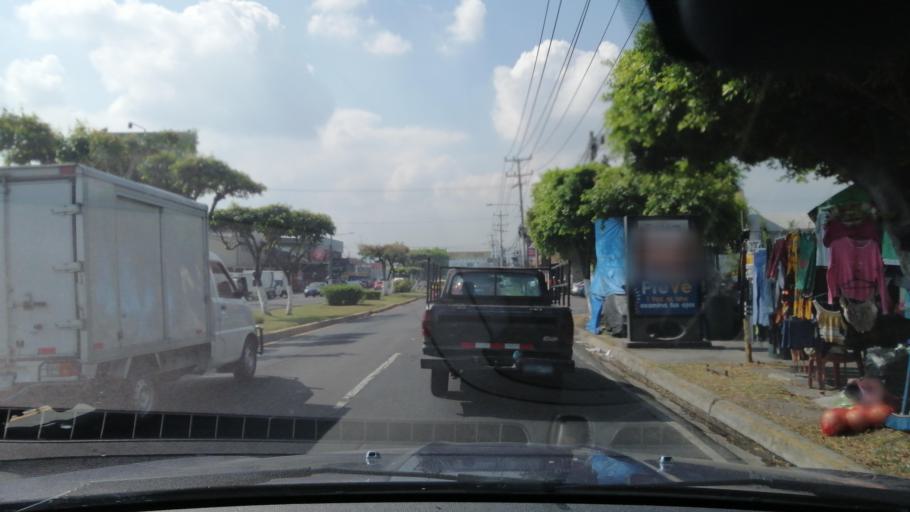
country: SV
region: San Salvador
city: Mejicanos
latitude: 13.7229
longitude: -89.2223
